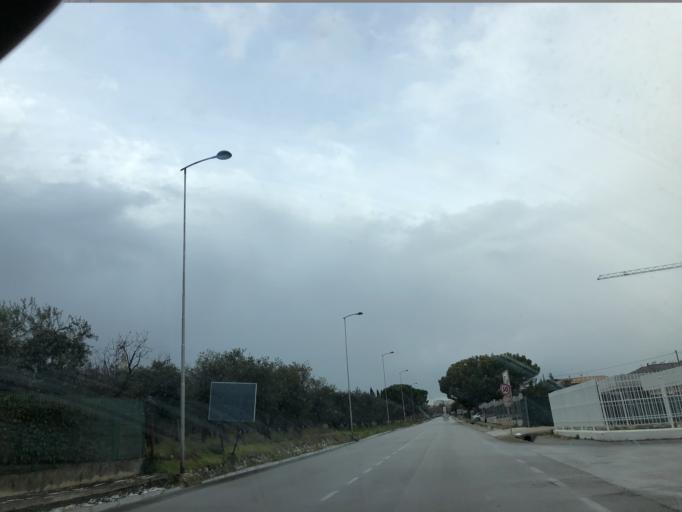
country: IT
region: Apulia
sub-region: Provincia di Foggia
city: Lucera
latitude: 41.5022
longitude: 15.3527
